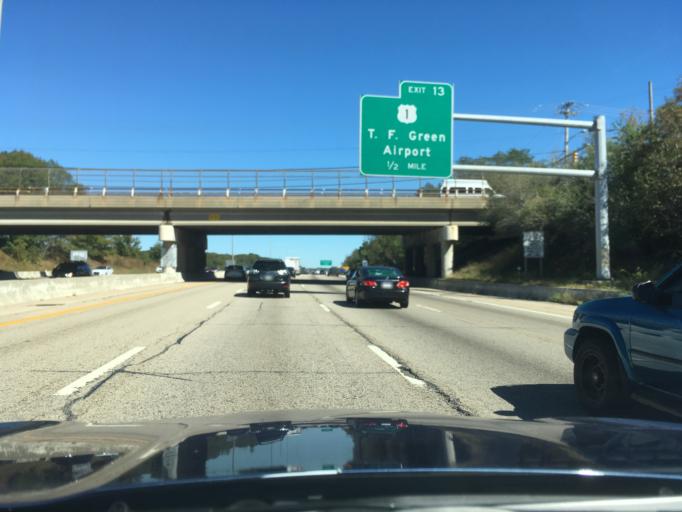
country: US
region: Rhode Island
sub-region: Kent County
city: Warwick
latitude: 41.7217
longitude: -71.4675
